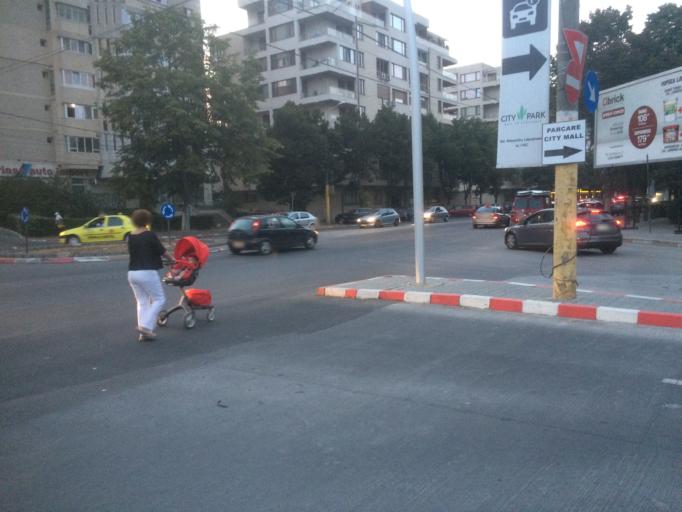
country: RO
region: Constanta
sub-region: Municipiul Constanta
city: Constanta
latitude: 44.2047
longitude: 28.6299
